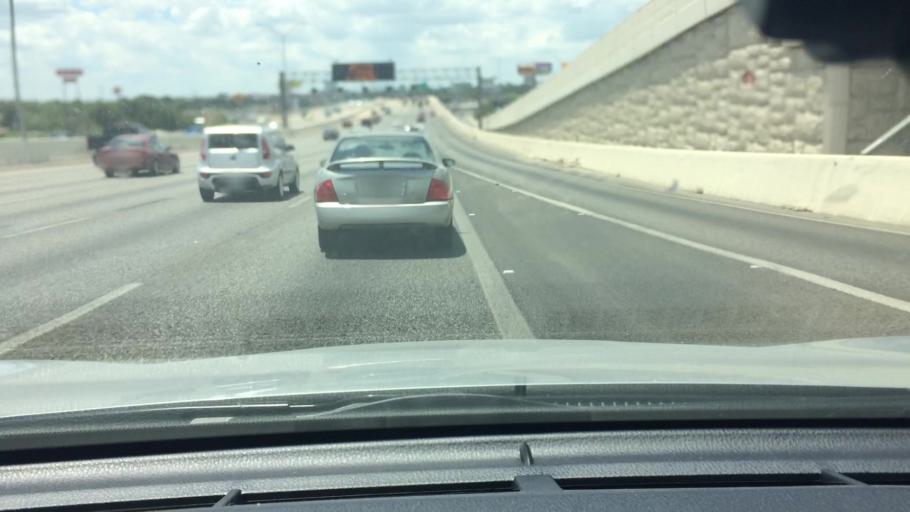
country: US
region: Texas
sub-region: Bexar County
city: Castle Hills
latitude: 29.5192
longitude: -98.5231
